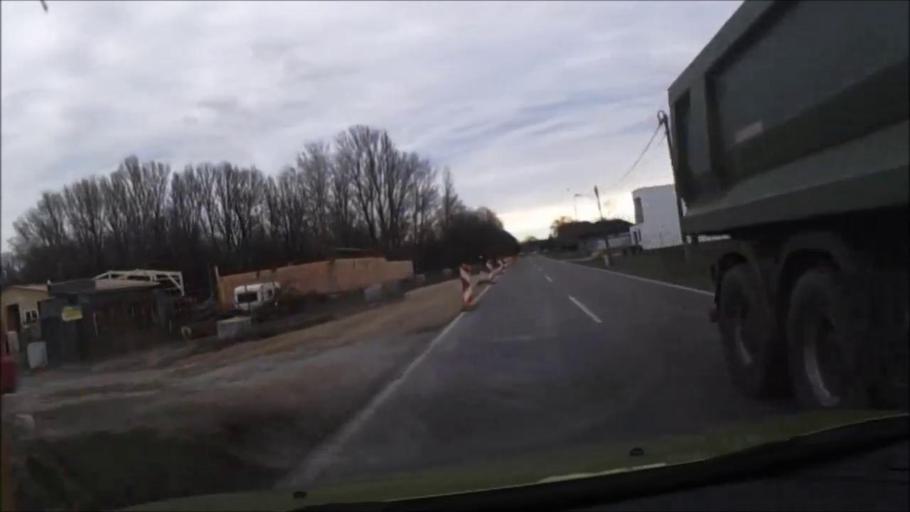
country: AT
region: Lower Austria
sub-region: Politischer Bezirk Baden
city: Ebreichsdorf
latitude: 47.9563
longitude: 16.4357
